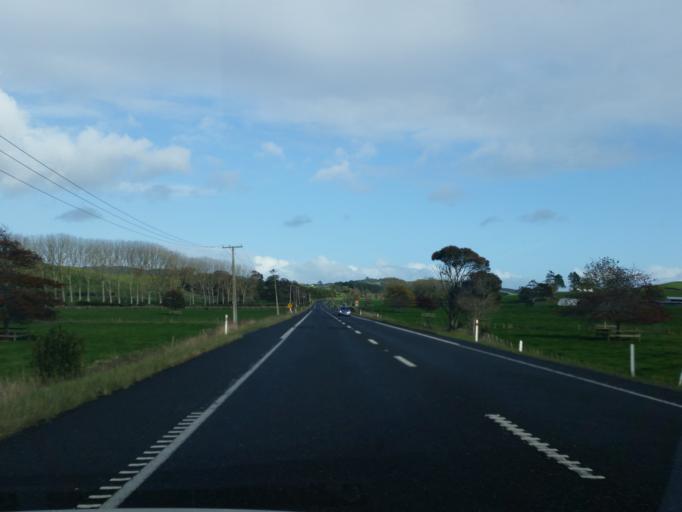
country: NZ
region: Waikato
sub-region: Hauraki District
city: Ngatea
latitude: -37.2858
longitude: 175.3933
